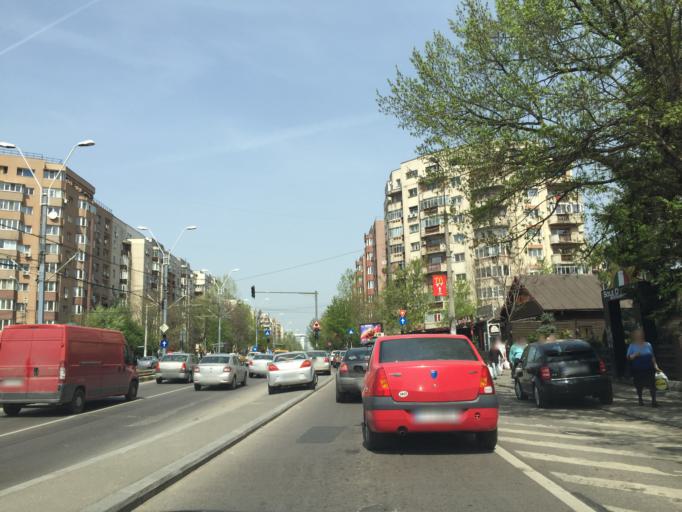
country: RO
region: Ilfov
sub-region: Comuna Chiajna
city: Rosu
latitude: 44.4358
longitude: 26.0353
